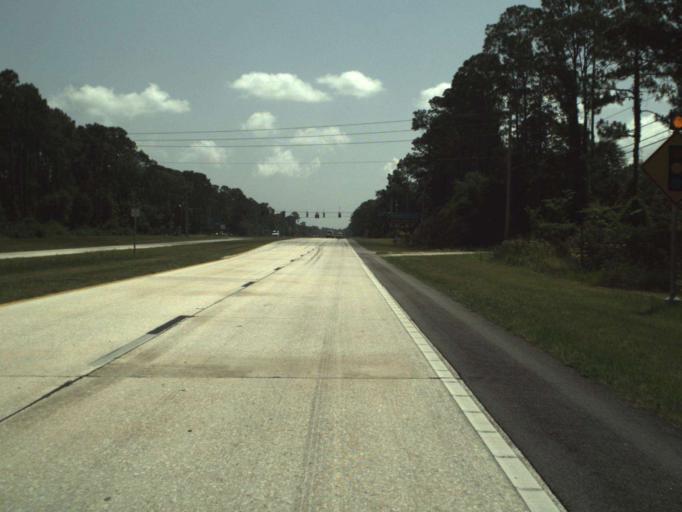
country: US
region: Florida
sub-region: Volusia County
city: Samsula-Spruce Creek
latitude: 29.1350
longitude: -81.1444
